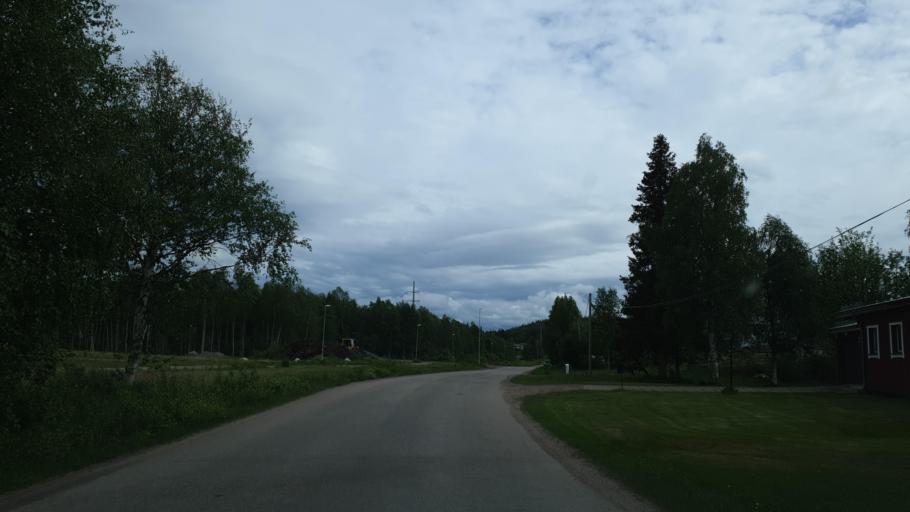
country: SE
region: Norrbotten
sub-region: Gallivare Kommun
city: Gaellivare
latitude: 67.1309
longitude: 20.6444
